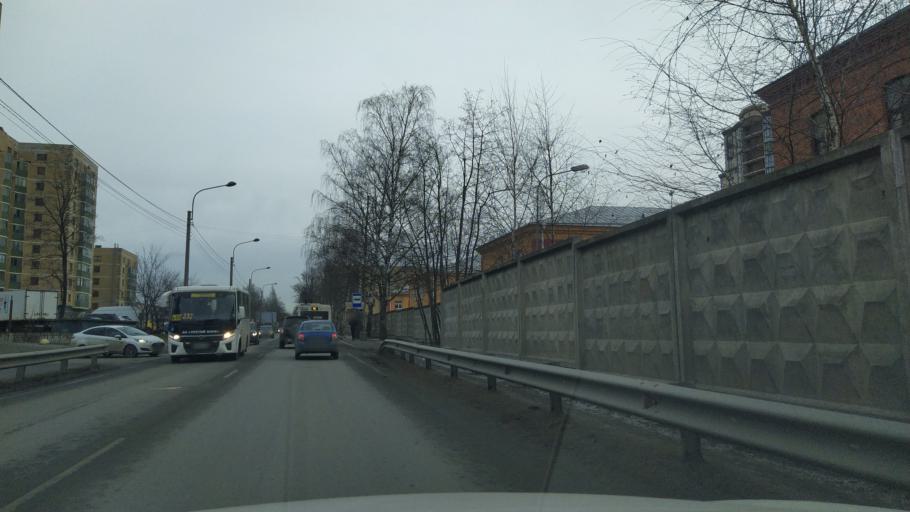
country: RU
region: Leningrad
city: Udel'naya
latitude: 60.0160
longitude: 30.3072
